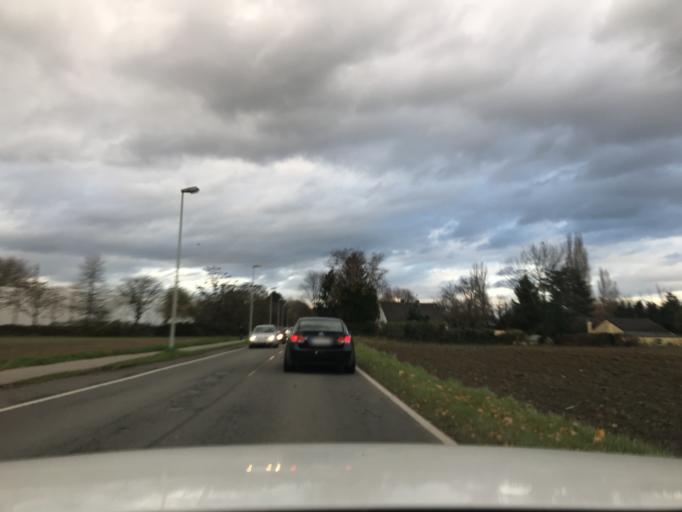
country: DE
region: North Rhine-Westphalia
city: Tonisvorst
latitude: 51.3347
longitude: 6.5301
